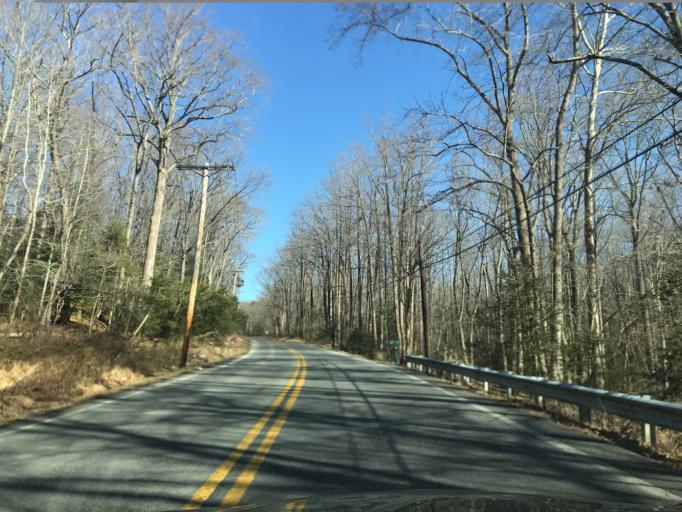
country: US
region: Maryland
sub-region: Charles County
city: Potomac Heights
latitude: 38.5926
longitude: -77.1041
